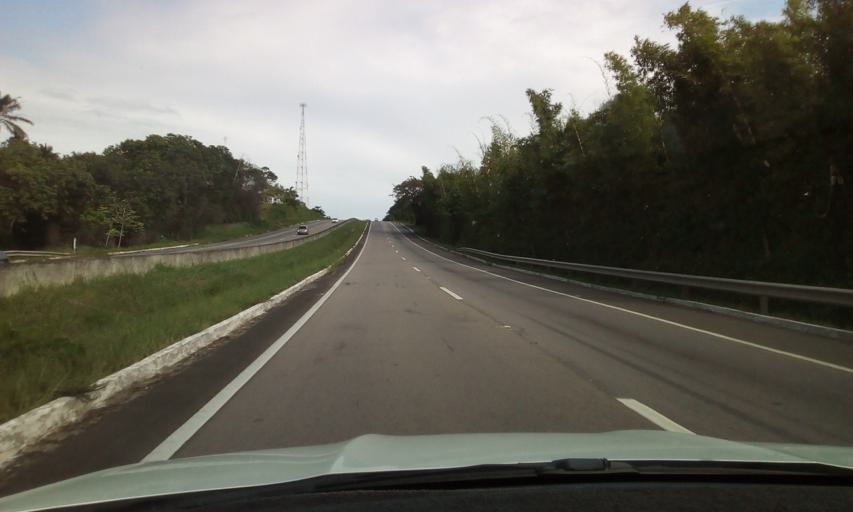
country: BR
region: Paraiba
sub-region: Conde
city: Conde
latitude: -7.3216
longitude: -34.9469
